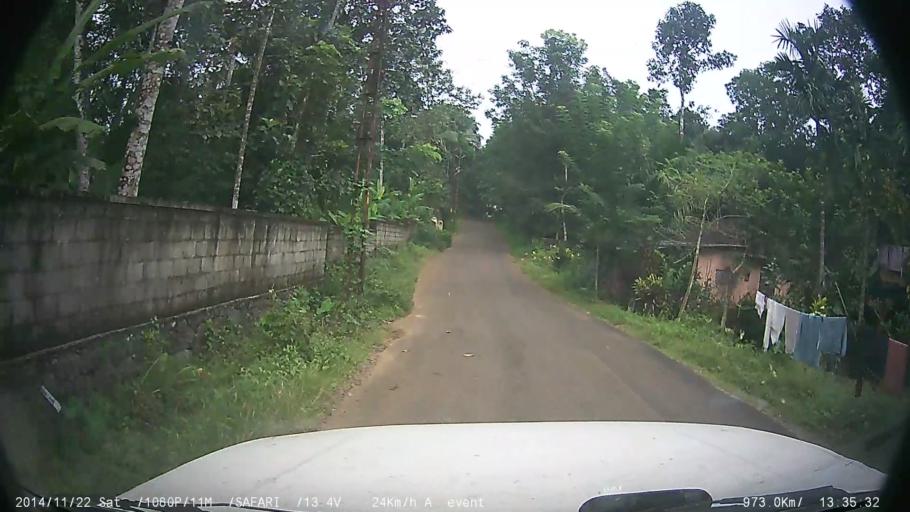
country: IN
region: Kerala
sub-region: Ernakulam
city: Piravam
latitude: 9.7937
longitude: 76.5395
